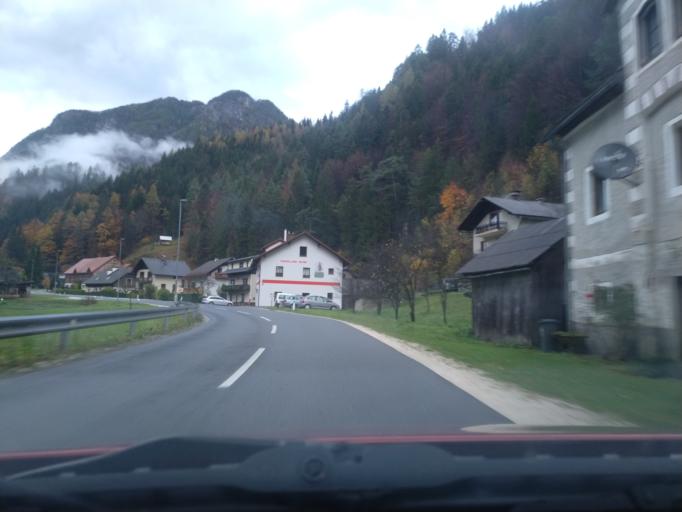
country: SI
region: Solcava
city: Solcava
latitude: 46.4185
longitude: 14.6972
